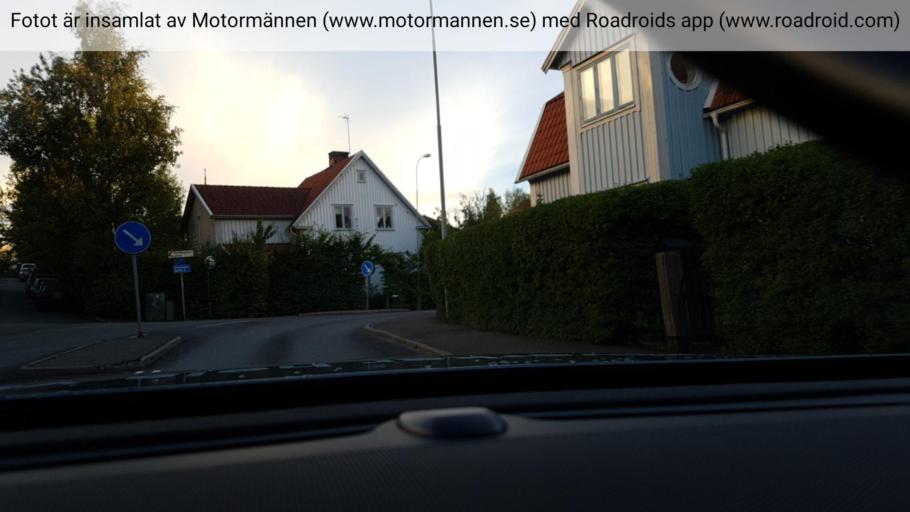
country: SE
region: Vaestra Goetaland
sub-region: Molndal
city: Moelndal
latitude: 57.6793
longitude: 11.9952
